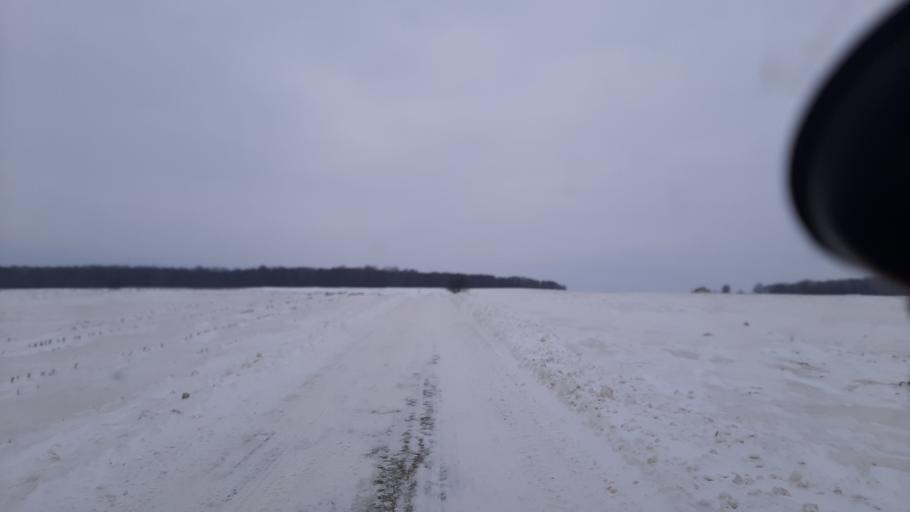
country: PL
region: Lublin Voivodeship
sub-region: Powiat lubelski
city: Garbow
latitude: 51.3229
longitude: 22.3103
